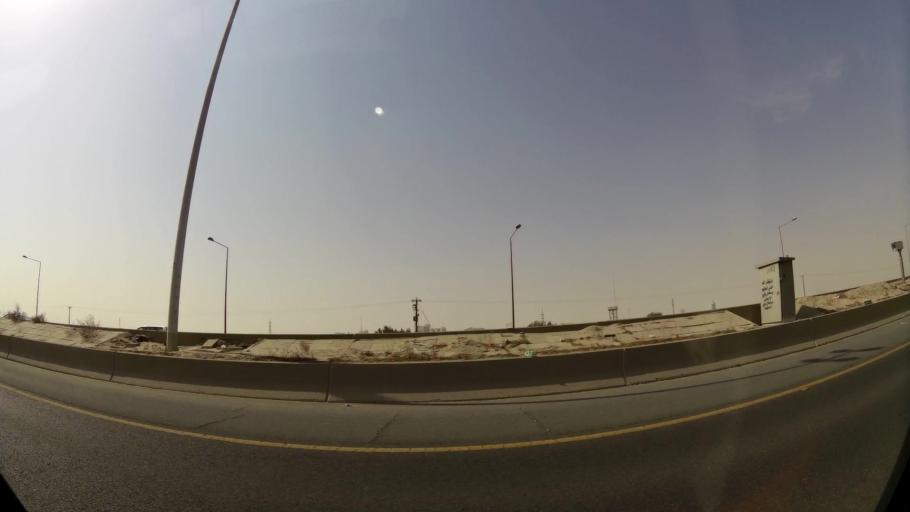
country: KW
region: Al Ahmadi
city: Al Fahahil
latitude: 29.0169
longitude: 48.1295
